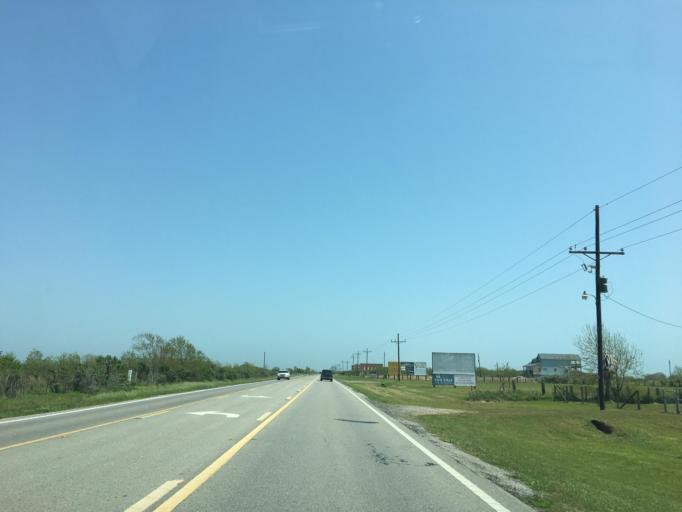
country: US
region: Texas
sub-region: Galveston County
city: Bolivar Peninsula
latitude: 29.4242
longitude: -94.6971
